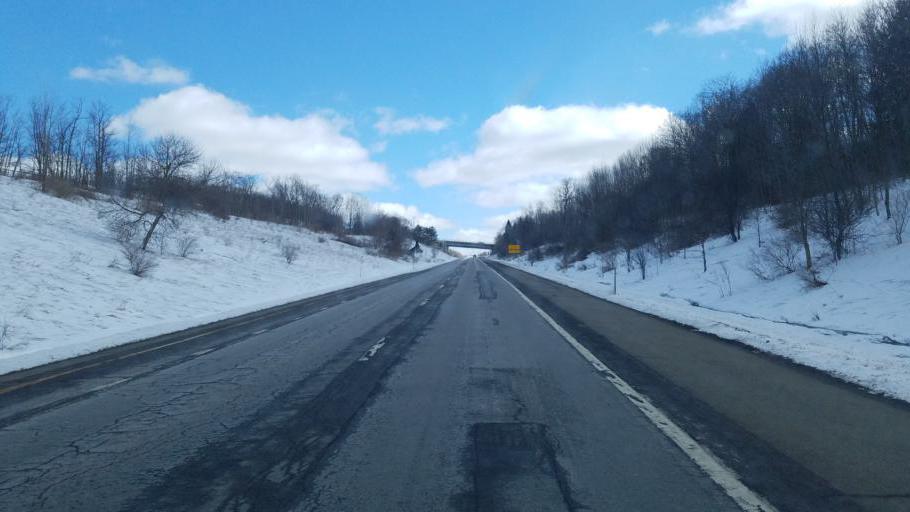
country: US
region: New York
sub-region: Chautauqua County
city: Lakewood
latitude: 42.1477
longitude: -79.3645
